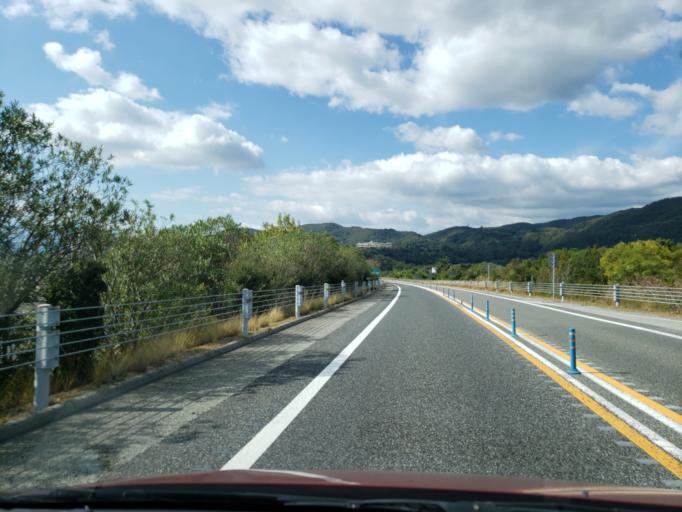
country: JP
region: Tokushima
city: Kamojimacho-jogejima
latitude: 34.1185
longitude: 134.3329
